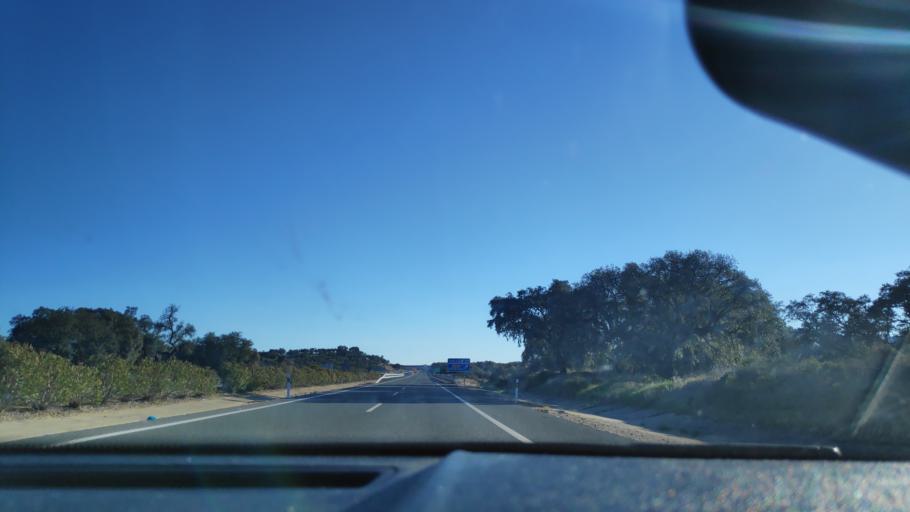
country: ES
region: Andalusia
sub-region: Provincia de Huelva
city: Santa Olalla del Cala
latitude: 37.9607
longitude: -6.2338
